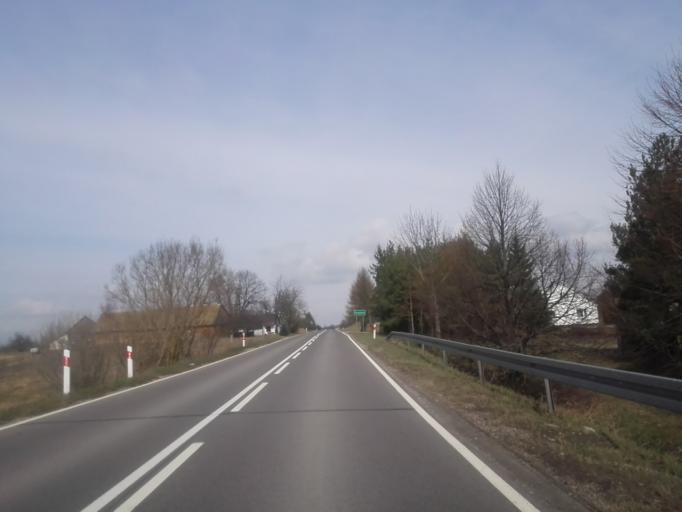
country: PL
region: Podlasie
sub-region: Powiat sejnenski
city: Sejny
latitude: 54.0735
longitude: 23.3510
